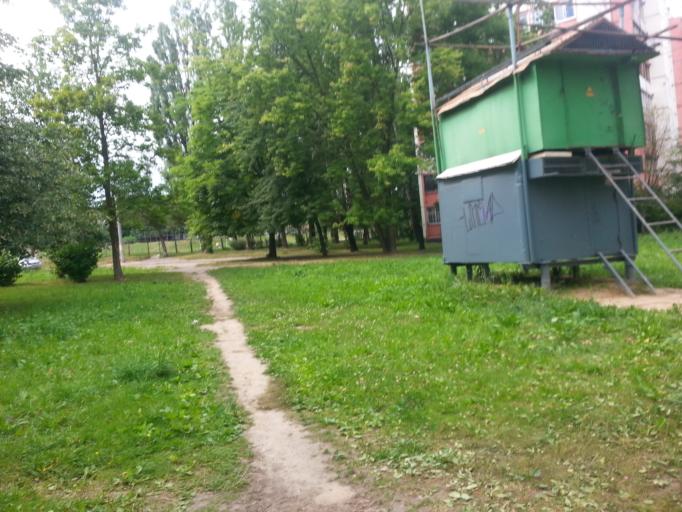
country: BY
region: Minsk
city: Novoye Medvezhino
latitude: 53.9137
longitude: 27.4922
